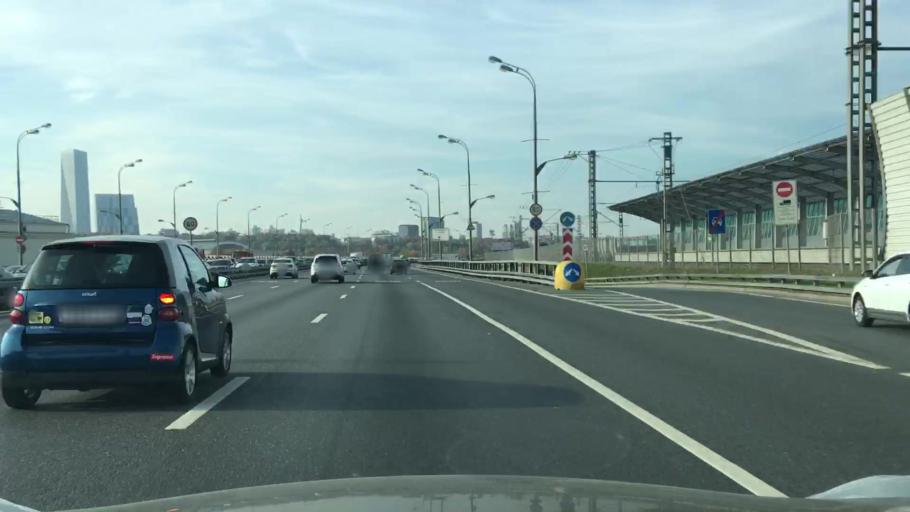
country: RU
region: Moscow
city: Luzhniki
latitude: 55.7236
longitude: 37.5583
